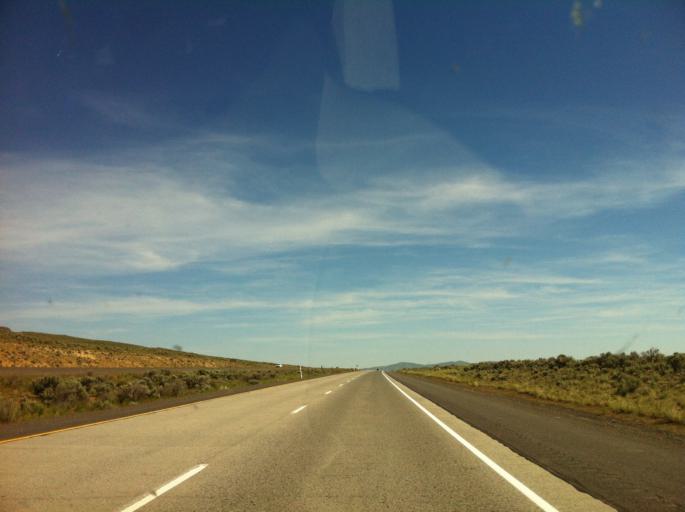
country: US
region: Oregon
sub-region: Union County
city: Union
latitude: 45.0984
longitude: -117.9540
